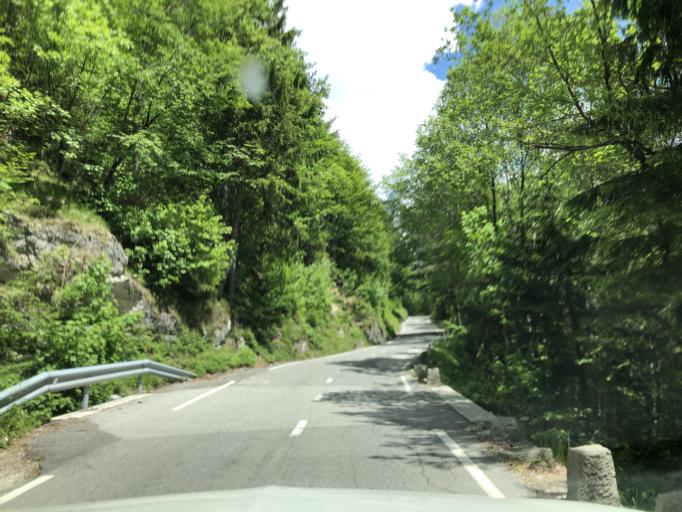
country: IT
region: Friuli Venezia Giulia
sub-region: Provincia di Udine
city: Tarvisio
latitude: 46.4136
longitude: 13.6165
